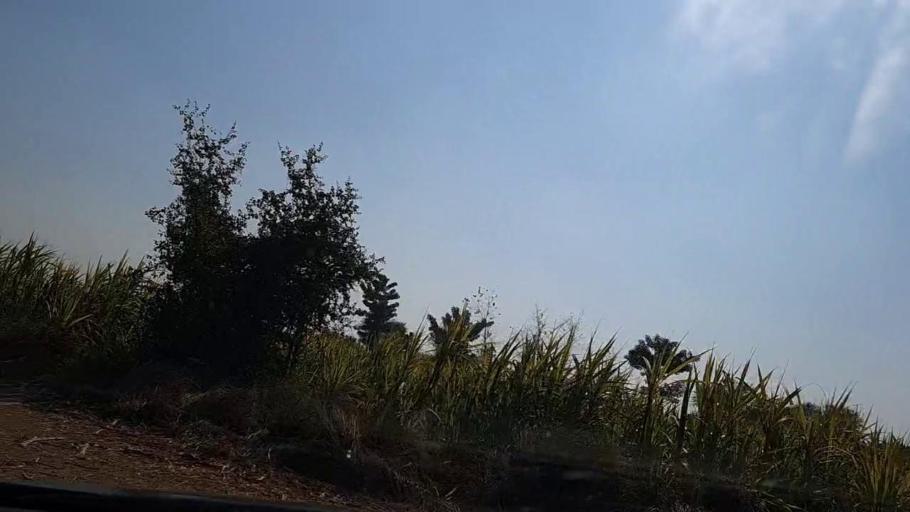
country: PK
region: Sindh
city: Nawabshah
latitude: 26.2279
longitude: 68.3137
